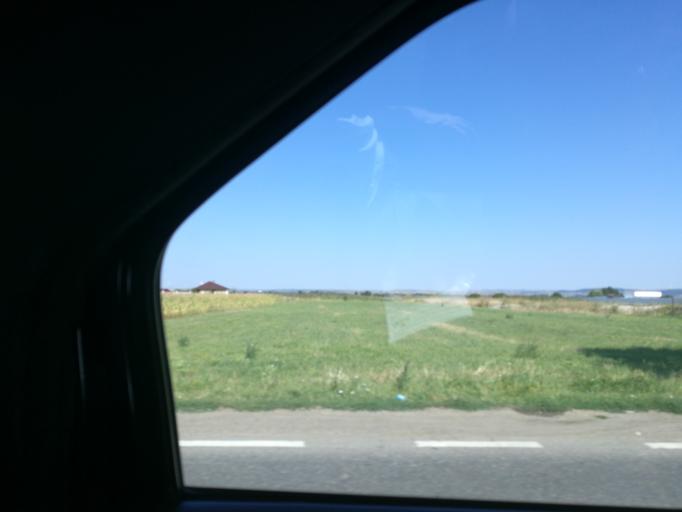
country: RO
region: Suceava
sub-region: Municipiul Suceava
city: Radauti
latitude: 47.8266
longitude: 25.9392
